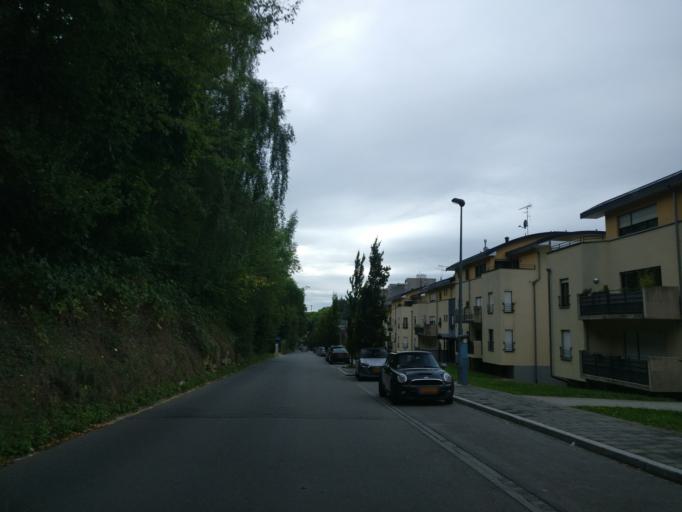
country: LU
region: Luxembourg
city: Kirchberg
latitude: 49.6256
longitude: 6.1442
